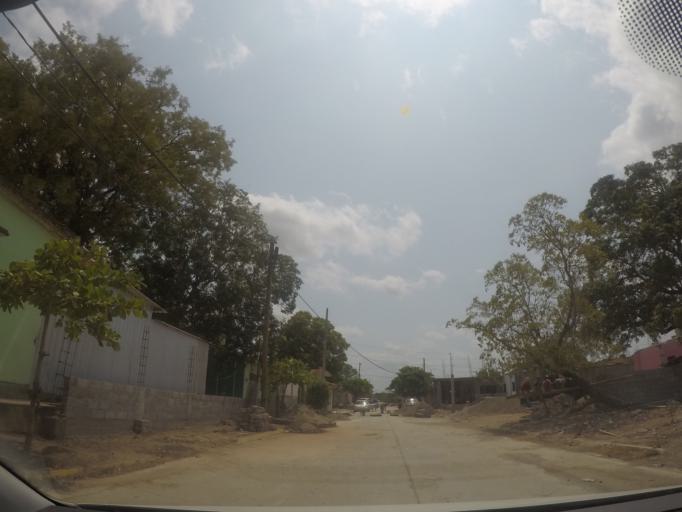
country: MX
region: Oaxaca
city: Asuncion Ixtaltepec
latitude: 16.5016
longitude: -95.0607
